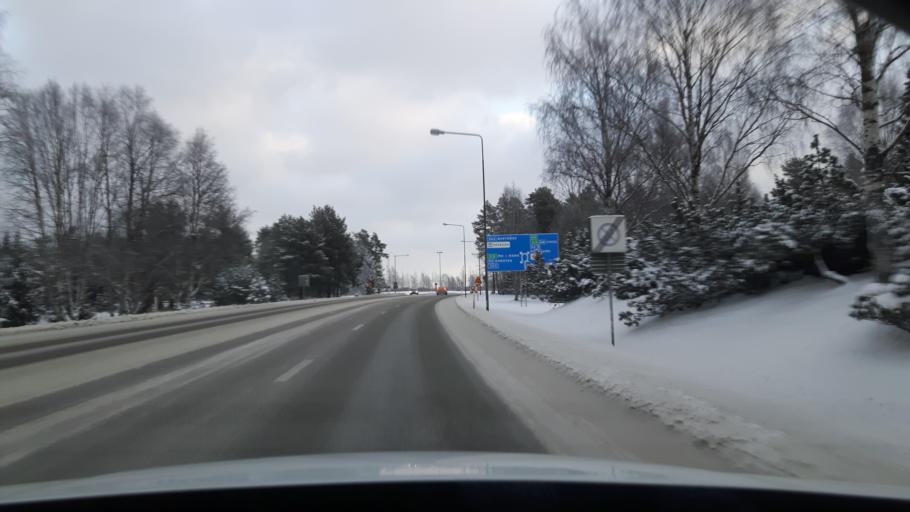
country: SE
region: Vaesterbotten
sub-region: Umea Kommun
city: Umea
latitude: 63.8486
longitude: 20.2904
